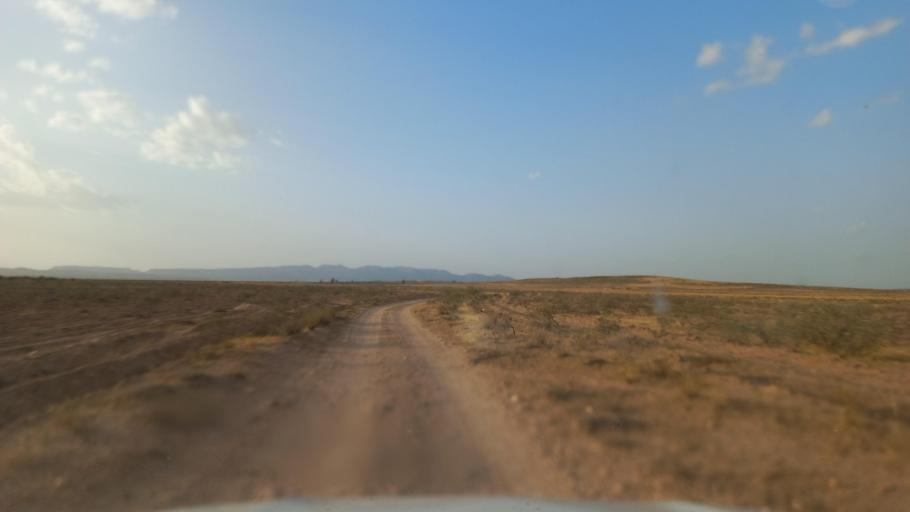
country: TN
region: Al Qasrayn
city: Sbiba
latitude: 35.3035
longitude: 9.0751
